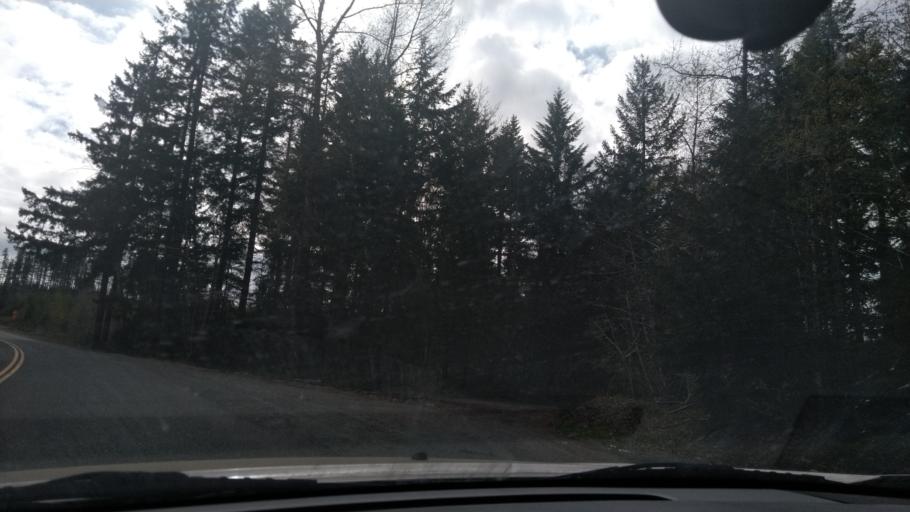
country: CA
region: British Columbia
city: Campbell River
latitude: 50.0009
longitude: -125.3725
